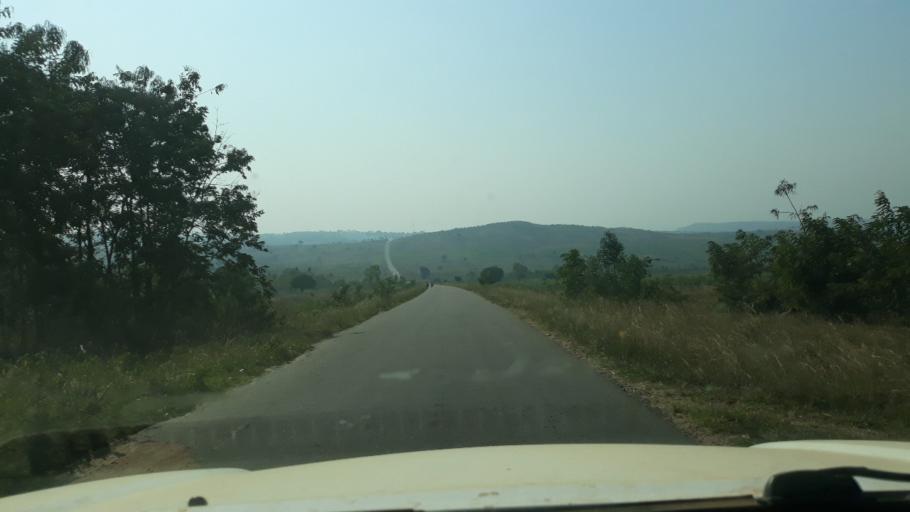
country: BI
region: Cibitoke
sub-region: Commune of Buganda
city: Buganda
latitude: -3.0200
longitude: 29.1071
